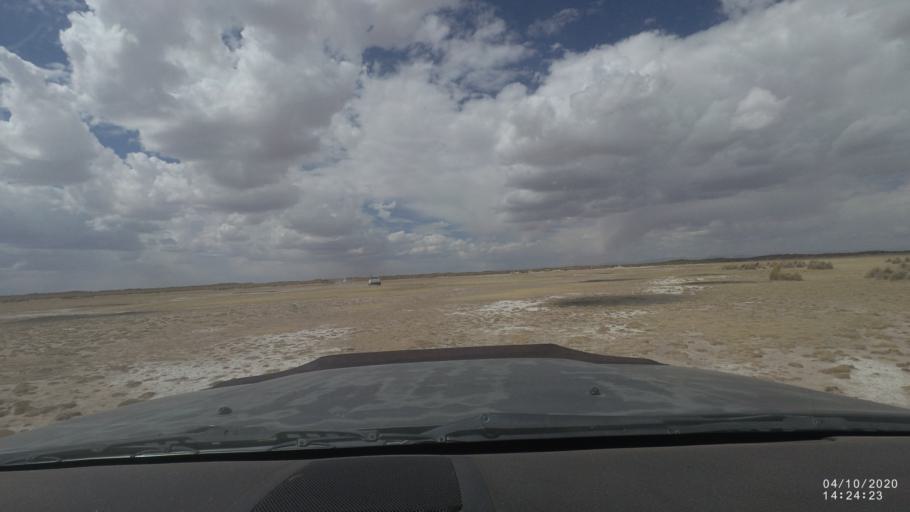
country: BO
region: Oruro
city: Poopo
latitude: -18.6769
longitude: -67.4508
